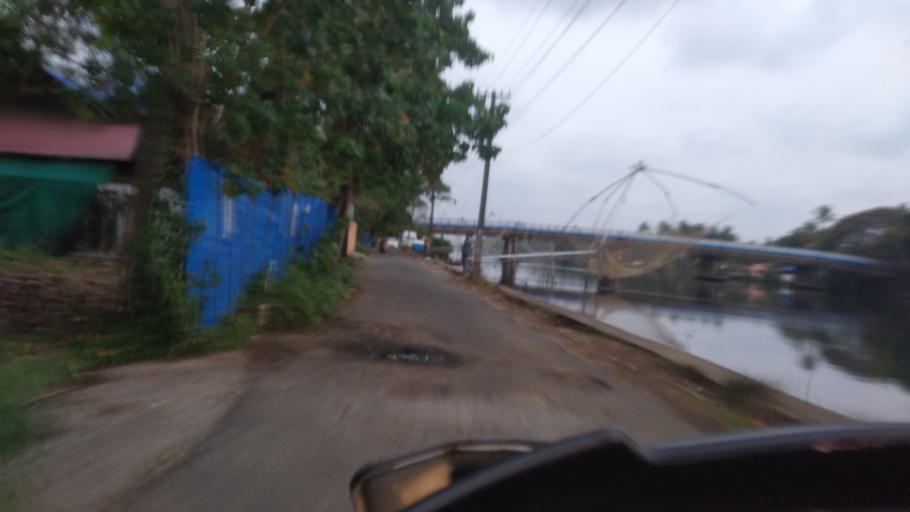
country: IN
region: Kerala
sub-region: Thrissur District
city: Kodungallur
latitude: 10.1415
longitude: 76.2015
